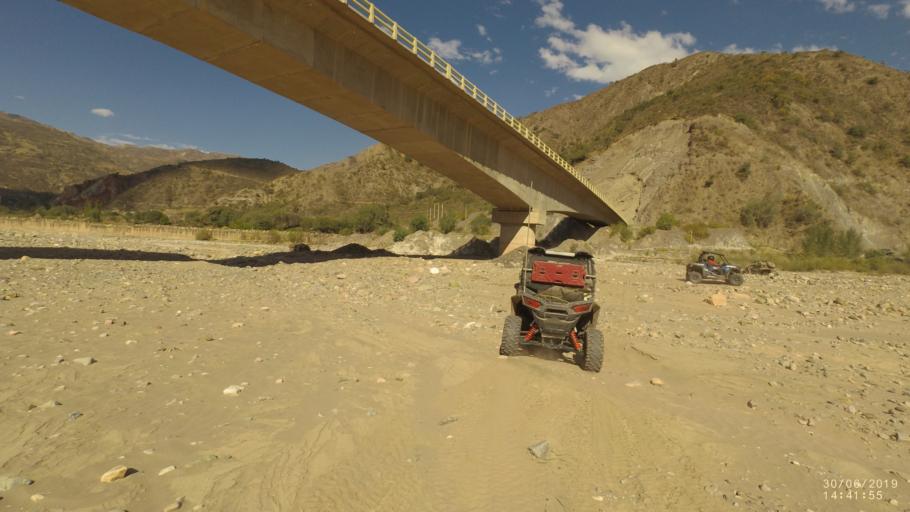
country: BO
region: Cochabamba
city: Irpa Irpa
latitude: -17.7998
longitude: -66.3505
